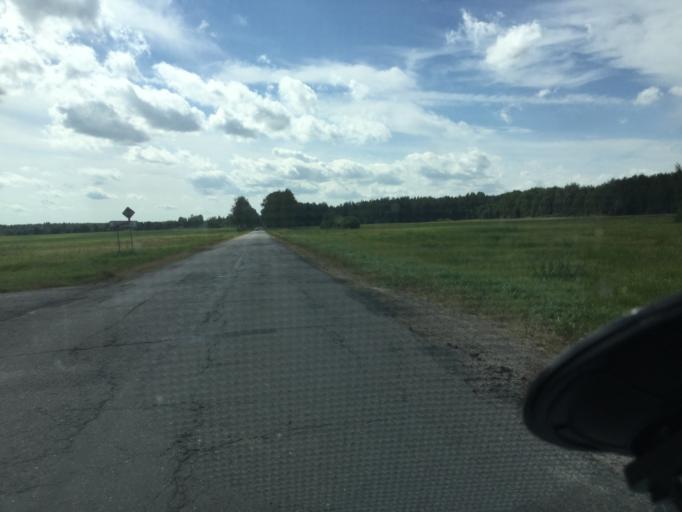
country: BY
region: Vitebsk
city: Chashniki
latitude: 55.3093
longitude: 29.4052
